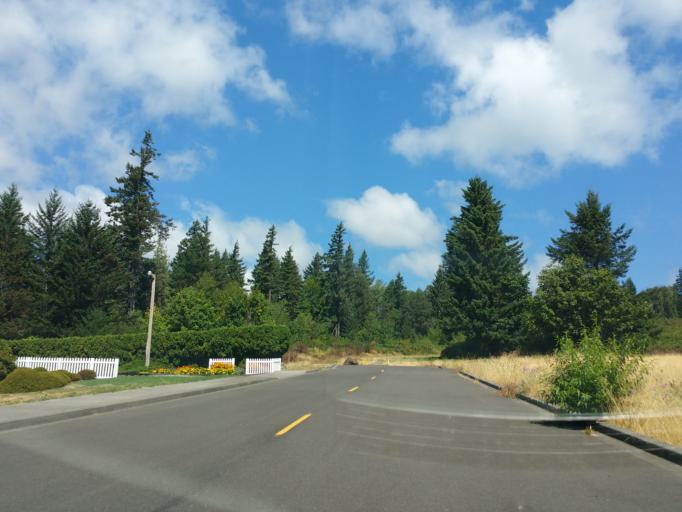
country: US
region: Washington
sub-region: Skamania County
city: Stevenson
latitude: 45.6986
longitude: -121.8768
